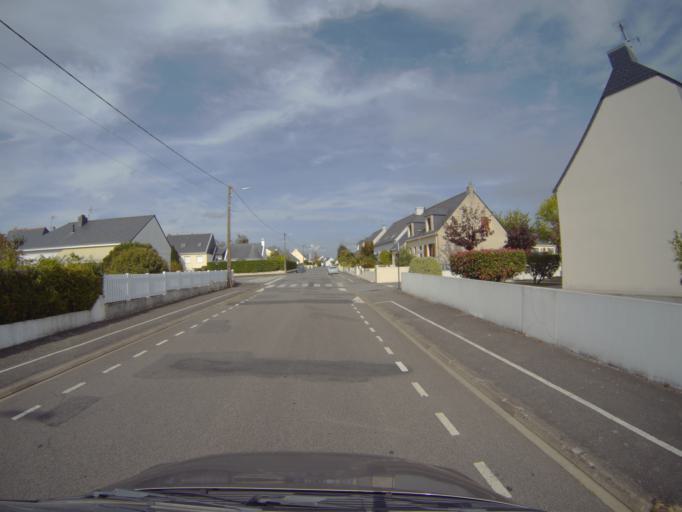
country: FR
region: Pays de la Loire
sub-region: Departement de la Loire-Atlantique
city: Saint-Herblain
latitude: 47.2128
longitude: -1.6441
